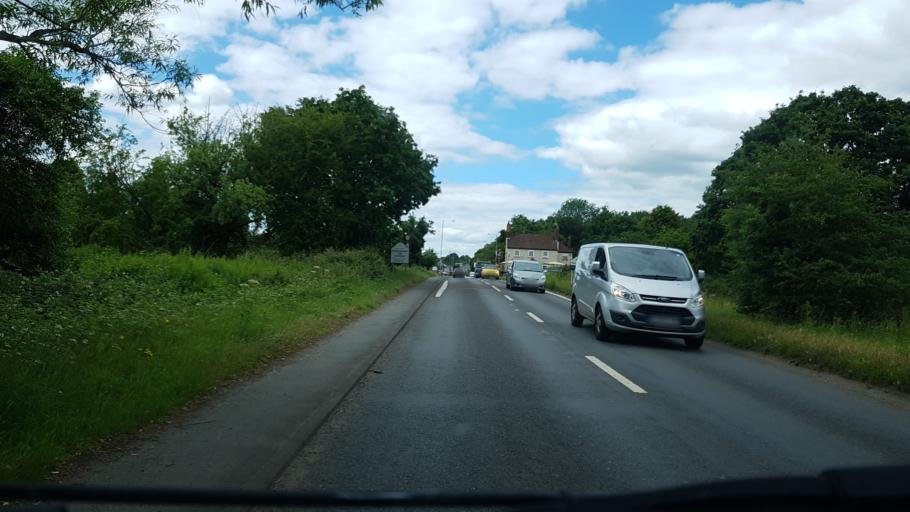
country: GB
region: England
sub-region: Worcestershire
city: Stourport-on-Severn
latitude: 52.3351
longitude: -2.2679
